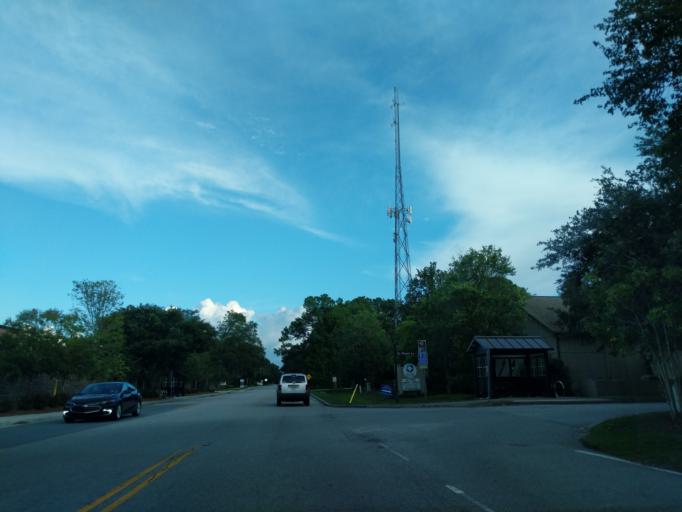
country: US
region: South Carolina
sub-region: Charleston County
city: Isle of Palms
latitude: 32.8407
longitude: -79.8160
